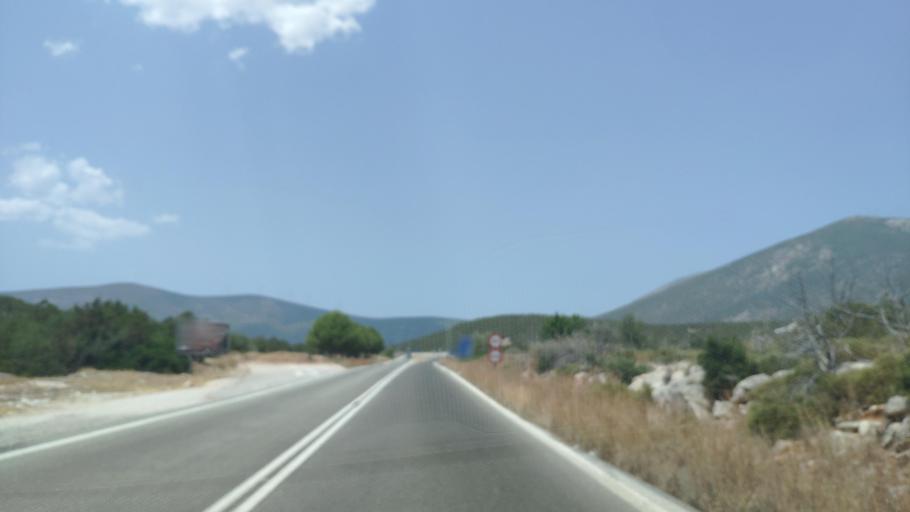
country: GR
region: Peloponnese
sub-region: Nomos Argolidos
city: Didyma
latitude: 37.4409
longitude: 23.1859
